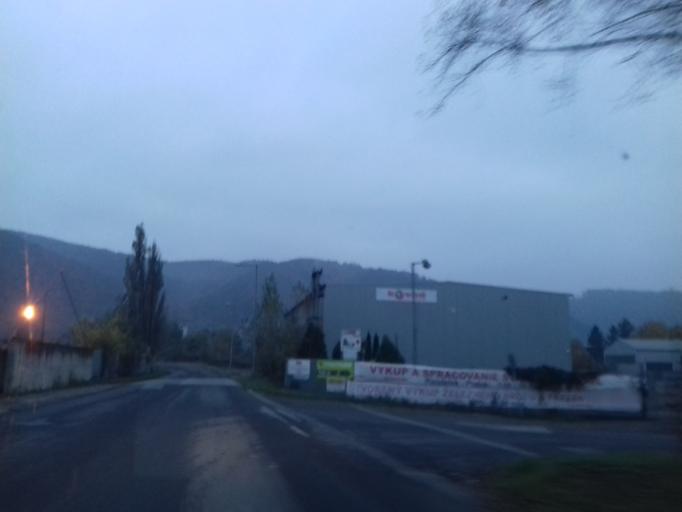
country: SK
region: Banskobystricky
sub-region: Okres Banska Bystrica
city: Banska Bystrica
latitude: 48.7395
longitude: 19.1781
